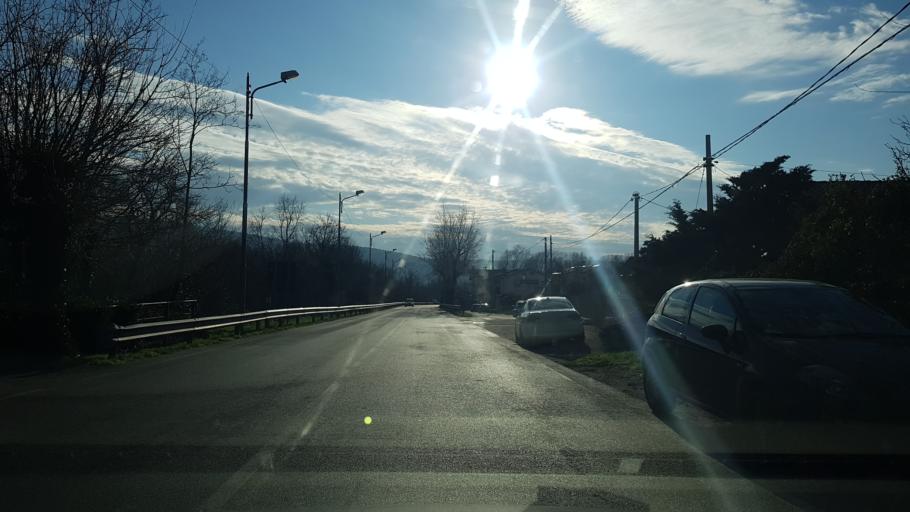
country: IT
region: Friuli Venezia Giulia
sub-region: Provincia di Trieste
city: Dolina
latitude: 45.6084
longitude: 13.8555
